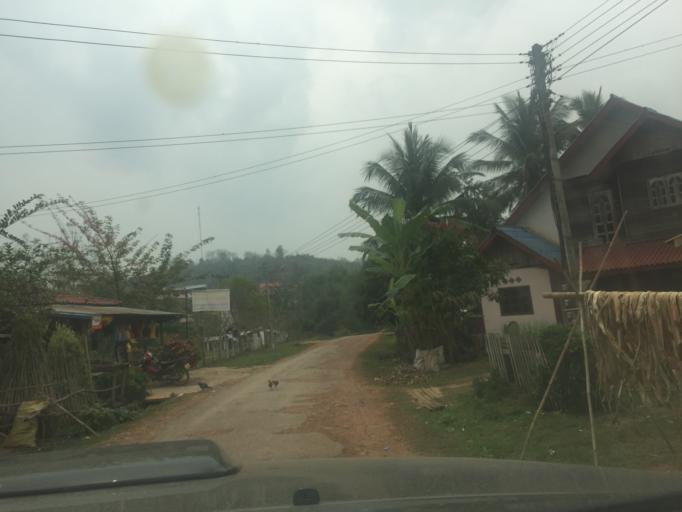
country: LA
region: Vientiane
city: Muang Sanakham
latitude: 18.4039
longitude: 101.5095
